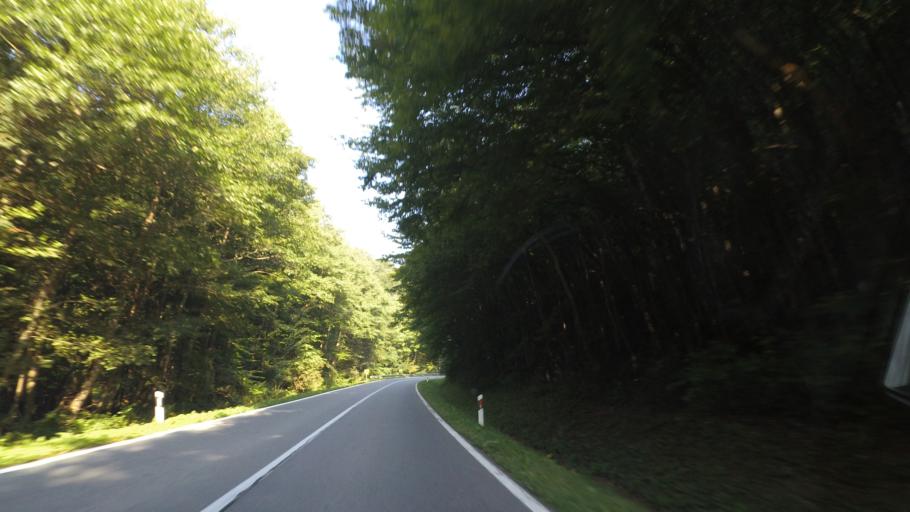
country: HR
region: Brodsko-Posavska
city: Cernik
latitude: 45.4533
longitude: 17.4619
